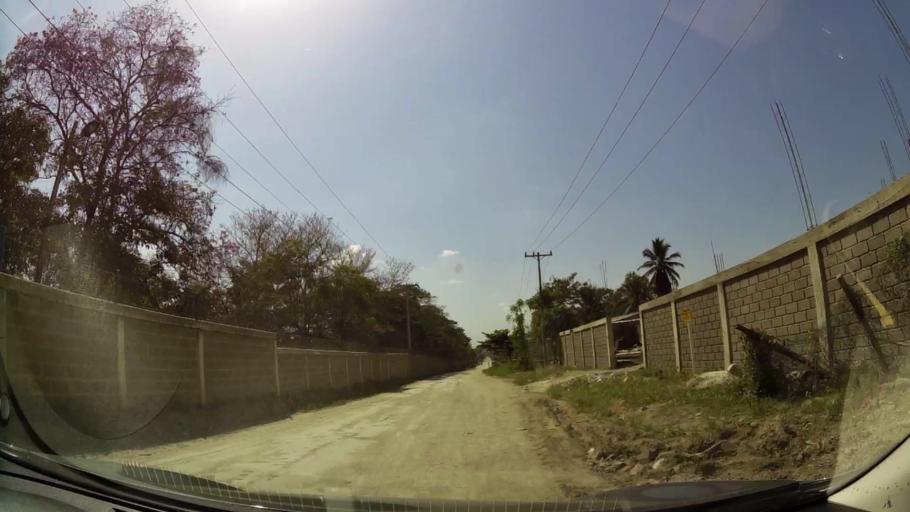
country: CO
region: Bolivar
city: Cartagena
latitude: 10.3572
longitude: -75.4887
